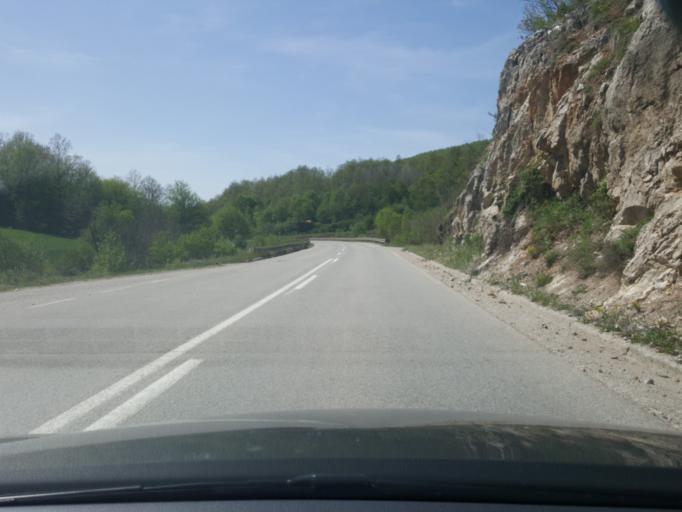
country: RS
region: Central Serbia
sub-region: Zlatiborski Okrug
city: Cajetina
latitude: 43.7881
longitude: 19.7201
